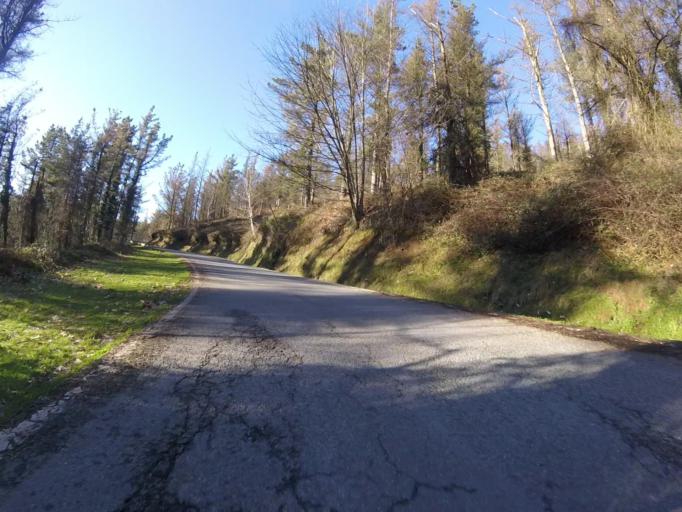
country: ES
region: Navarre
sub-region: Provincia de Navarra
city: Lesaka
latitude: 43.2664
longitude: -1.7408
